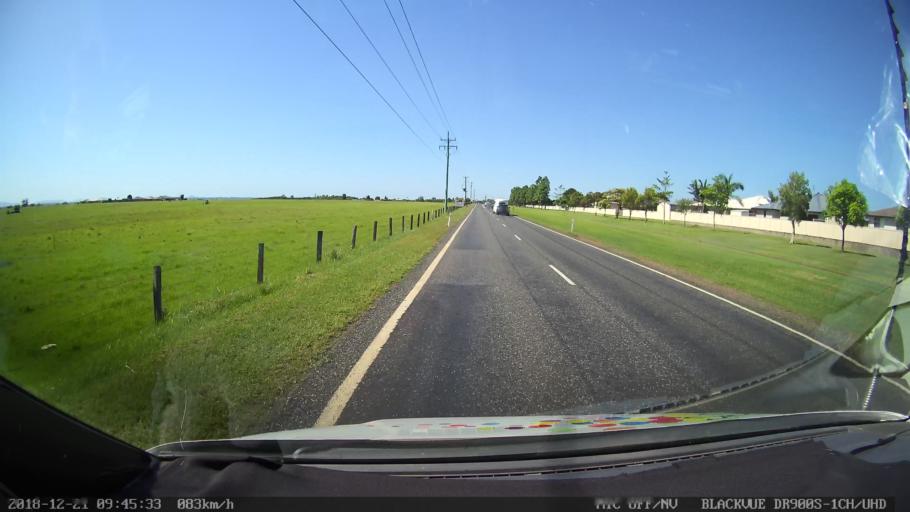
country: AU
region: New South Wales
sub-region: Clarence Valley
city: Grafton
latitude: -29.6300
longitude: 152.9284
